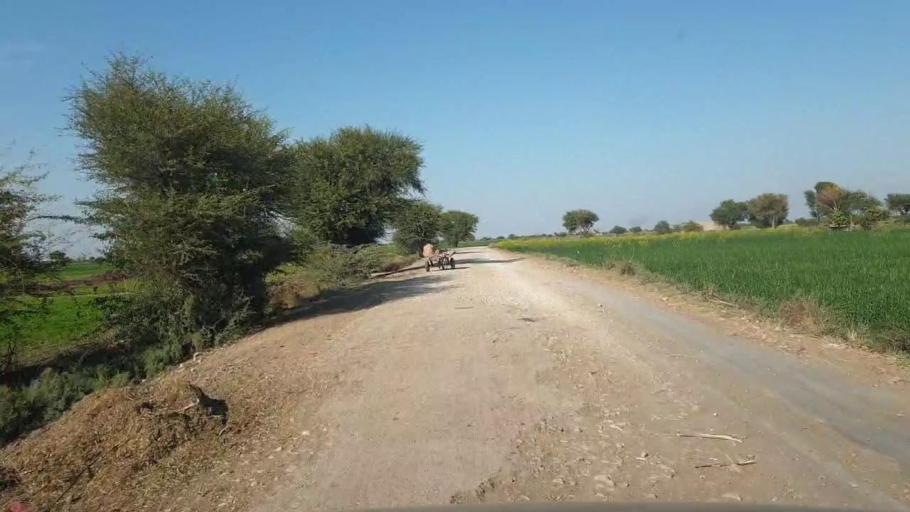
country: PK
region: Sindh
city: Shahpur Chakar
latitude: 26.1604
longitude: 68.6845
